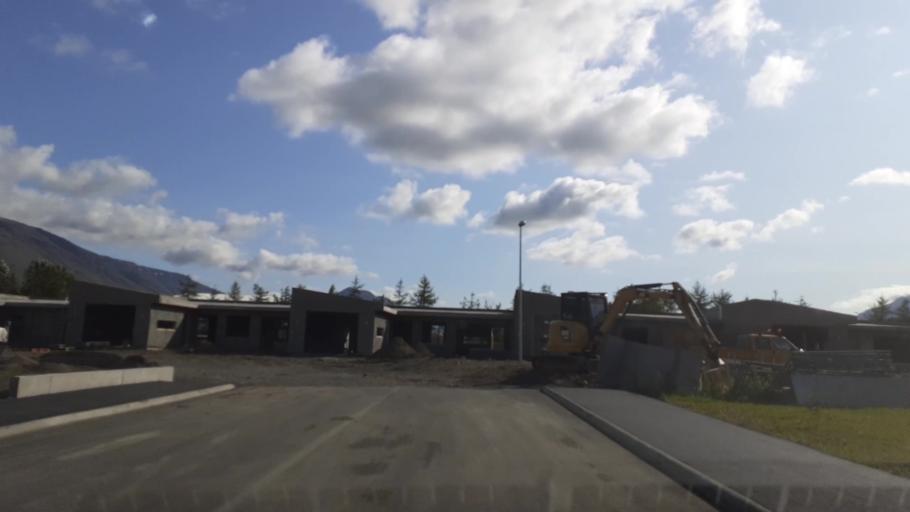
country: IS
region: Northeast
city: Akureyri
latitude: 65.5750
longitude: -18.0918
